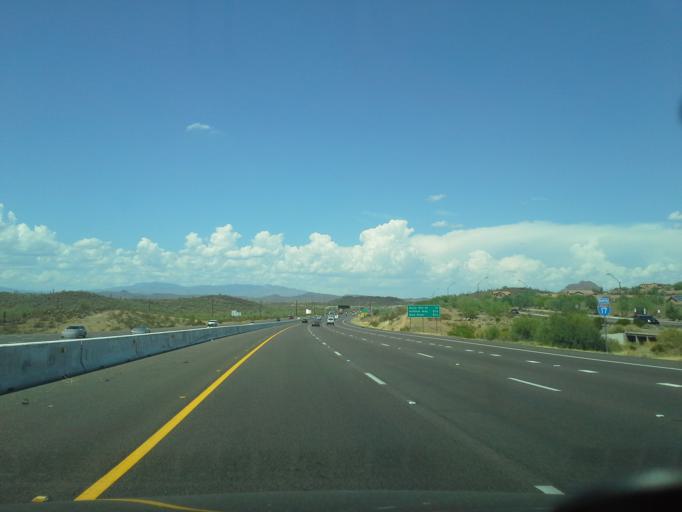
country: US
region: Arizona
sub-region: Maricopa County
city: Anthem
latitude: 33.8266
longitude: -112.1437
